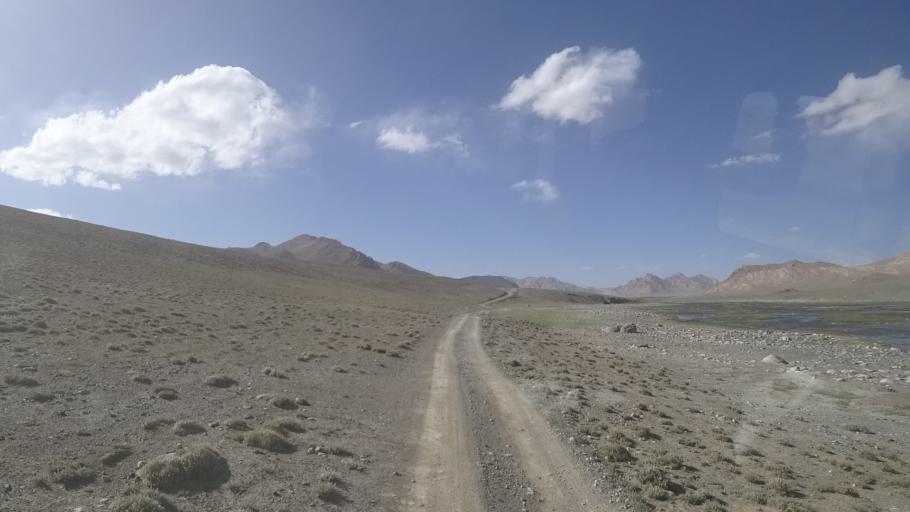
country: TJ
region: Gorno-Badakhshan
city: Murghob
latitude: 37.5730
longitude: 74.1585
